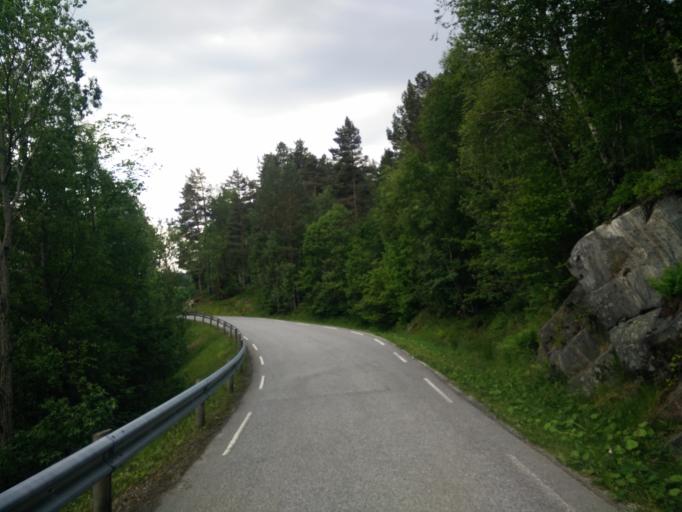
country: NO
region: More og Romsdal
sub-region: Kristiansund
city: Rensvik
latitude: 63.0268
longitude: 7.9533
